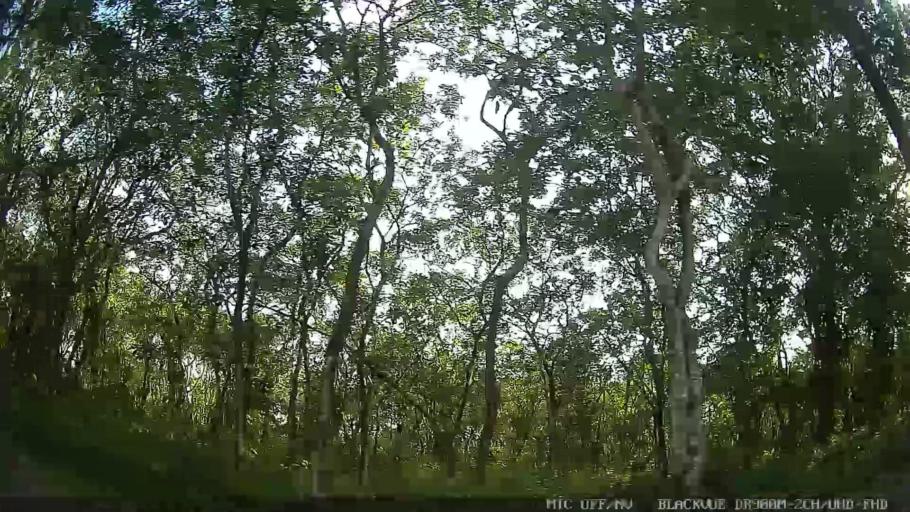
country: BR
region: Sao Paulo
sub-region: Cubatao
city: Cubatao
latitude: -23.9135
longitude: -46.4204
